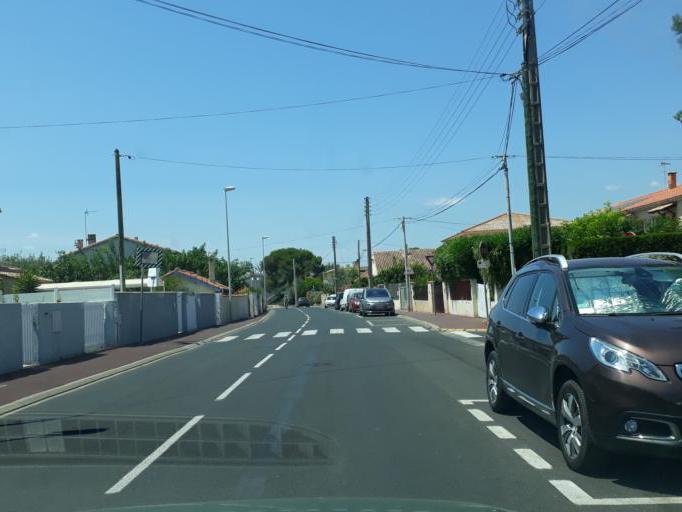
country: FR
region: Languedoc-Roussillon
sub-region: Departement de l'Herault
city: Agde
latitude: 43.2864
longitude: 3.4485
